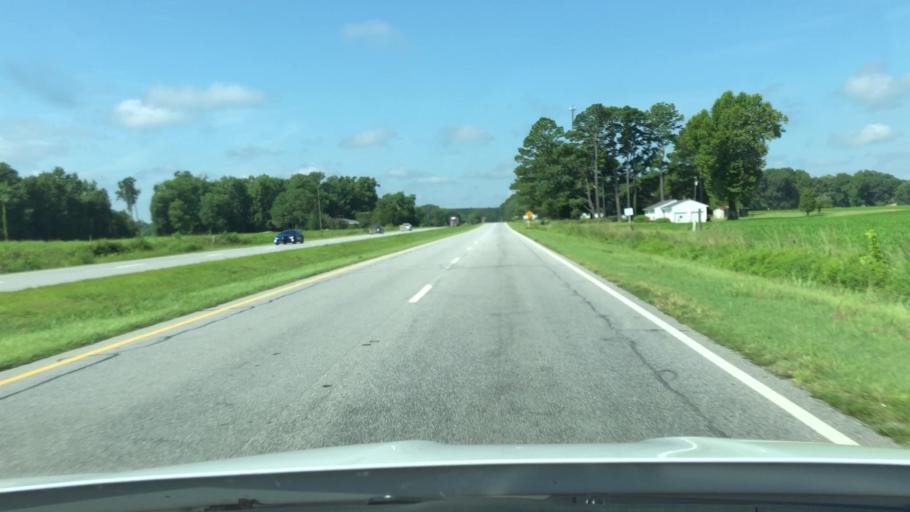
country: US
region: North Carolina
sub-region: Bertie County
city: Windsor
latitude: 35.9390
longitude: -76.9674
